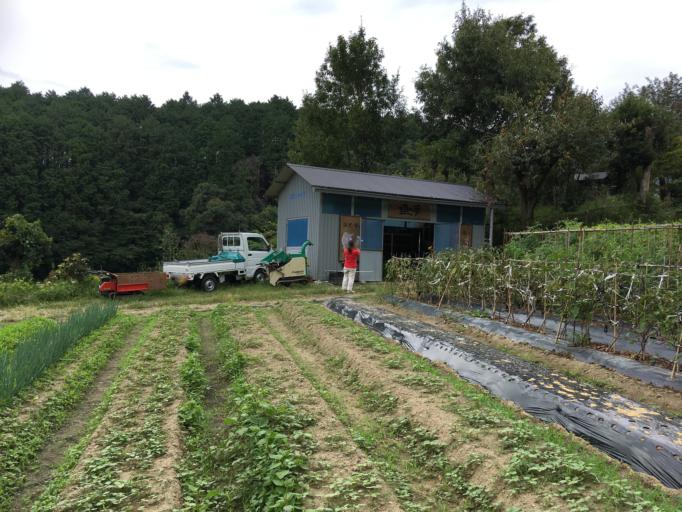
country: JP
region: Nara
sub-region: Ikoma-shi
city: Ikoma
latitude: 34.6722
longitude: 135.6982
